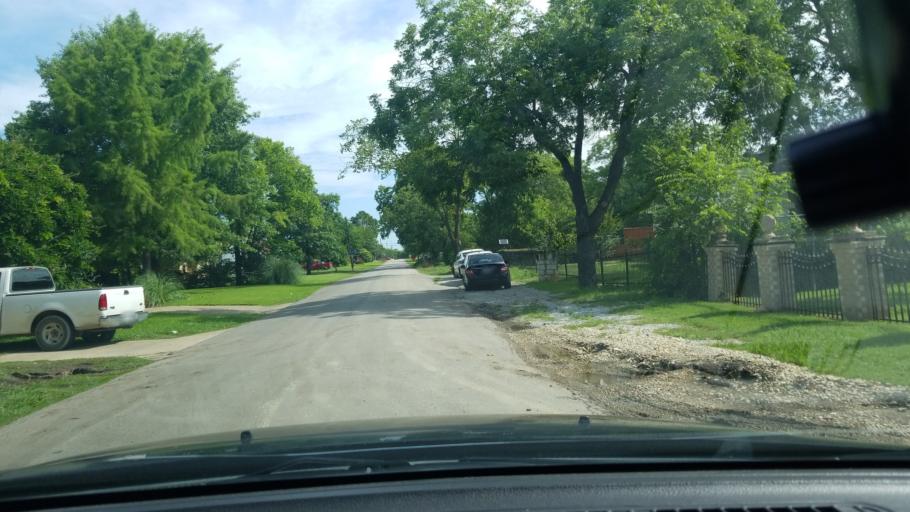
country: US
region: Texas
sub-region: Dallas County
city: Balch Springs
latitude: 32.7661
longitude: -96.6633
